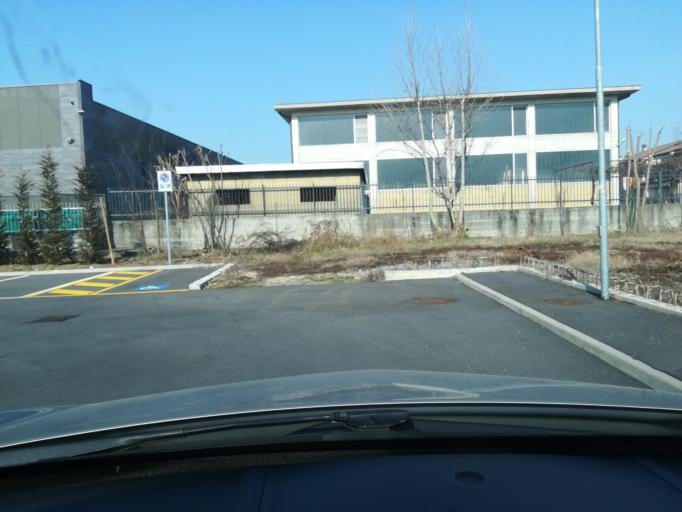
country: IT
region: Lombardy
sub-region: Provincia di Bergamo
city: Azzano San Paolo
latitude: 45.6541
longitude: 9.6638
